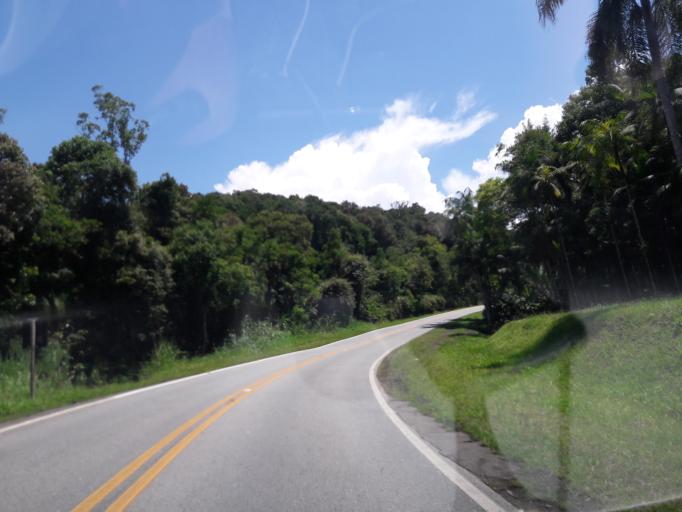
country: BR
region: Parana
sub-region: Antonina
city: Antonina
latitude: -25.5268
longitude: -48.7883
